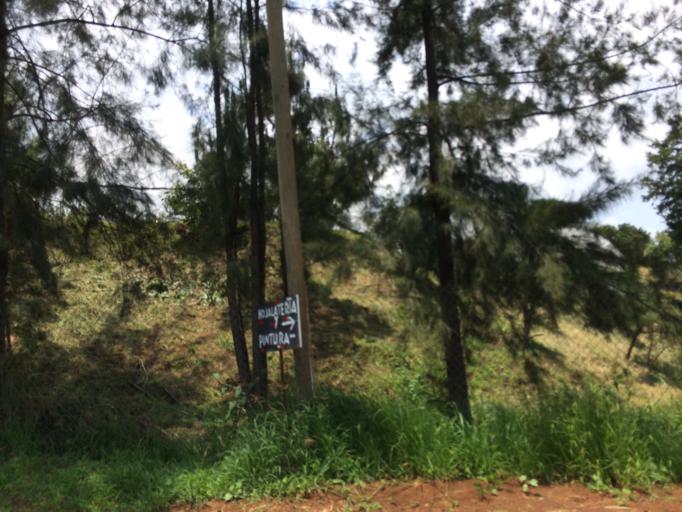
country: MX
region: Michoacan
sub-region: Periban
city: San Francisco Periban
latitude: 19.5420
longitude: -102.4089
